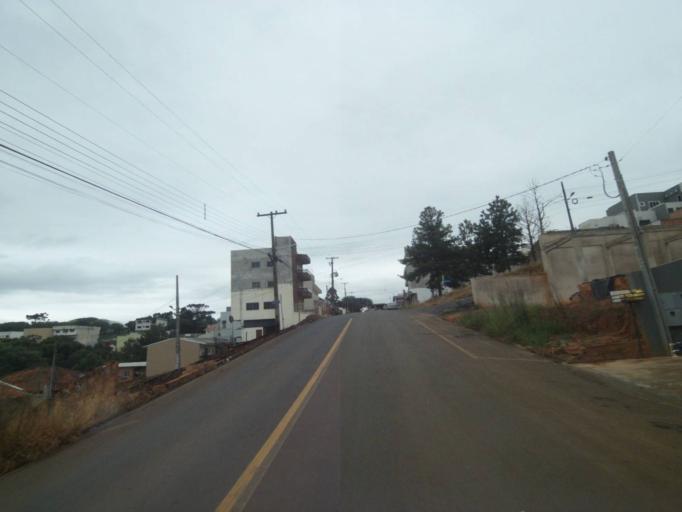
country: BR
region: Parana
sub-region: Telemaco Borba
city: Telemaco Borba
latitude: -24.3324
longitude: -50.6447
